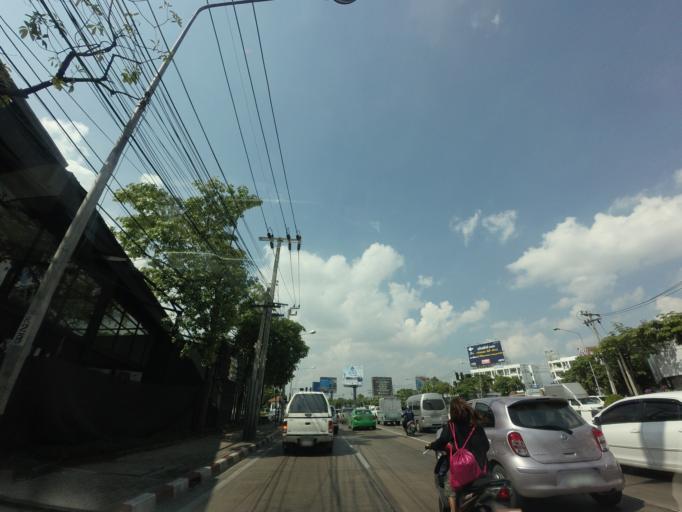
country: TH
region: Bangkok
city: Chatuchak
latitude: 13.8414
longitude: 100.5956
